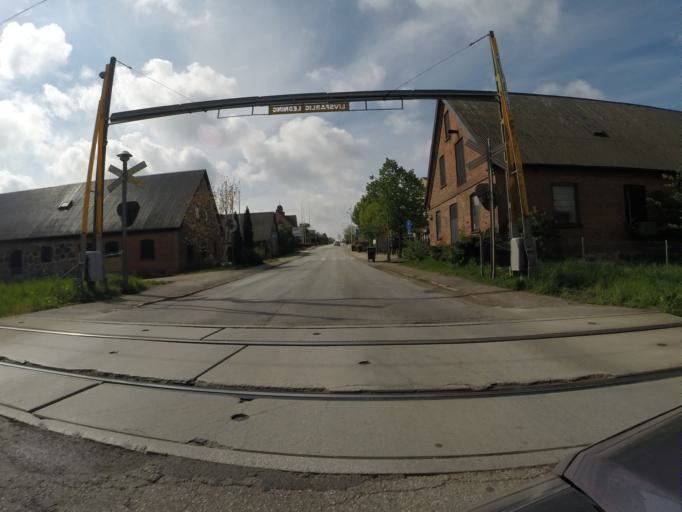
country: SE
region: Skane
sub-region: Landskrona
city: Asmundtorp
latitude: 55.9264
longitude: 12.9556
